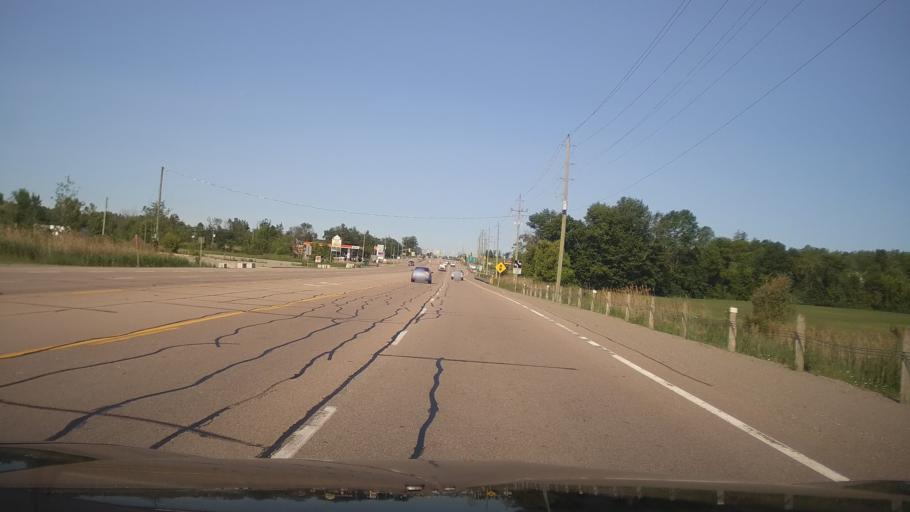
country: CA
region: Ontario
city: Peterborough
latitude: 44.2964
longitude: -78.2725
